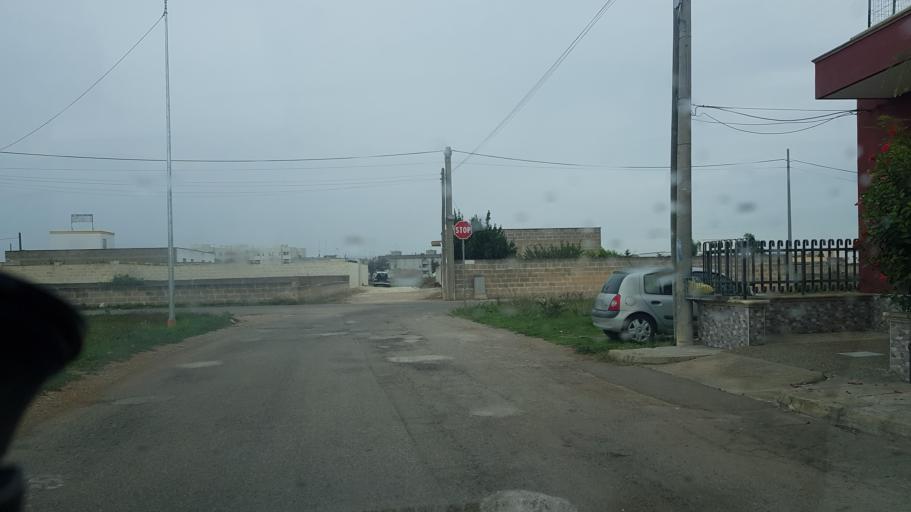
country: IT
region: Apulia
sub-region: Provincia di Lecce
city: Leverano
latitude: 40.2826
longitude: 17.9862
